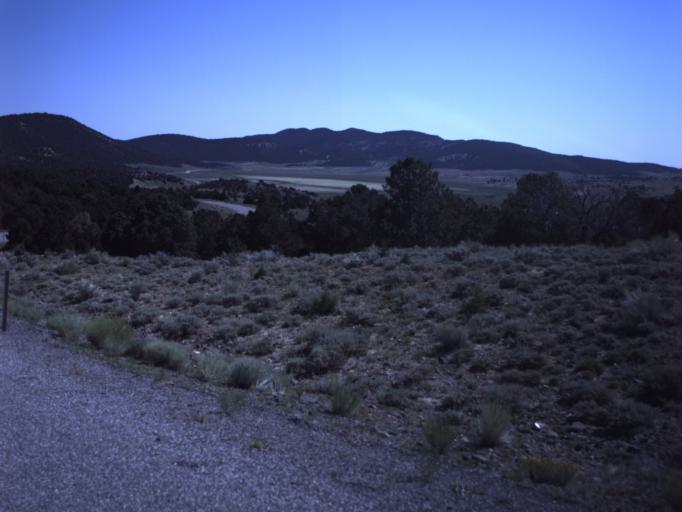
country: US
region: Utah
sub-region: Wayne County
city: Loa
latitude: 38.6164
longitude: -111.4593
